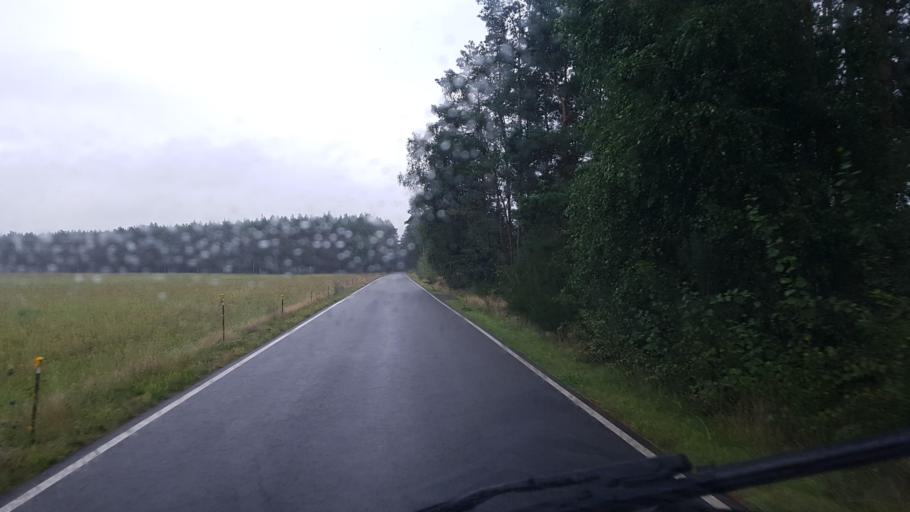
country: DE
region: Brandenburg
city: Lindenau
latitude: 51.4009
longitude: 13.7457
